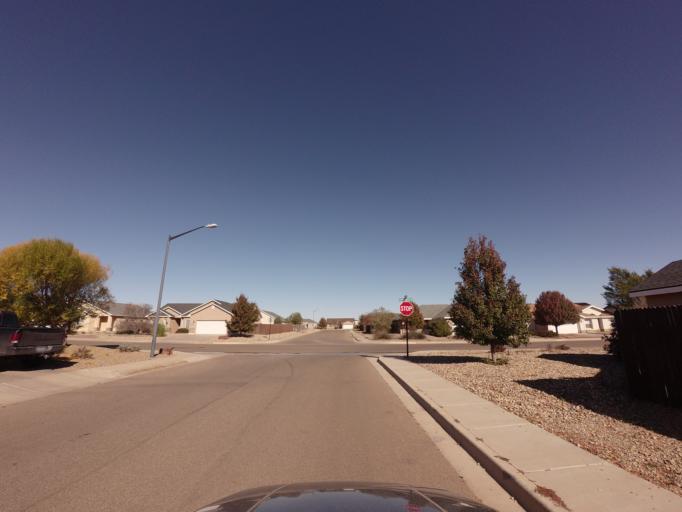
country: US
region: New Mexico
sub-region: Curry County
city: Clovis
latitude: 34.4144
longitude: -103.1623
